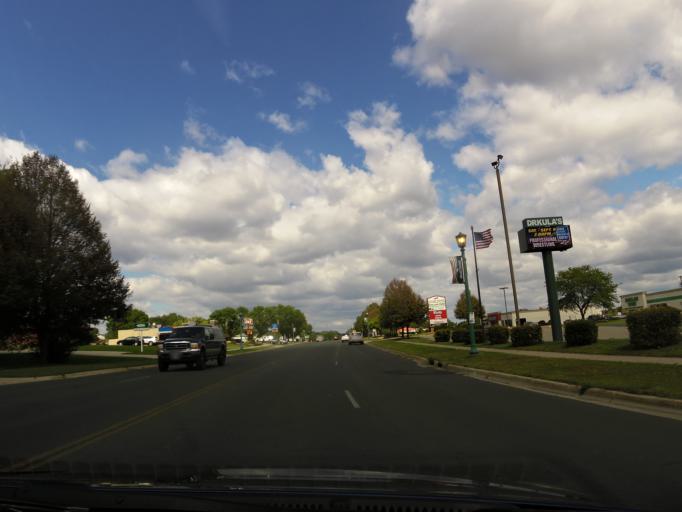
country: US
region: Minnesota
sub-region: Dakota County
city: Inver Grove Heights
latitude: 44.8518
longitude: -93.0449
